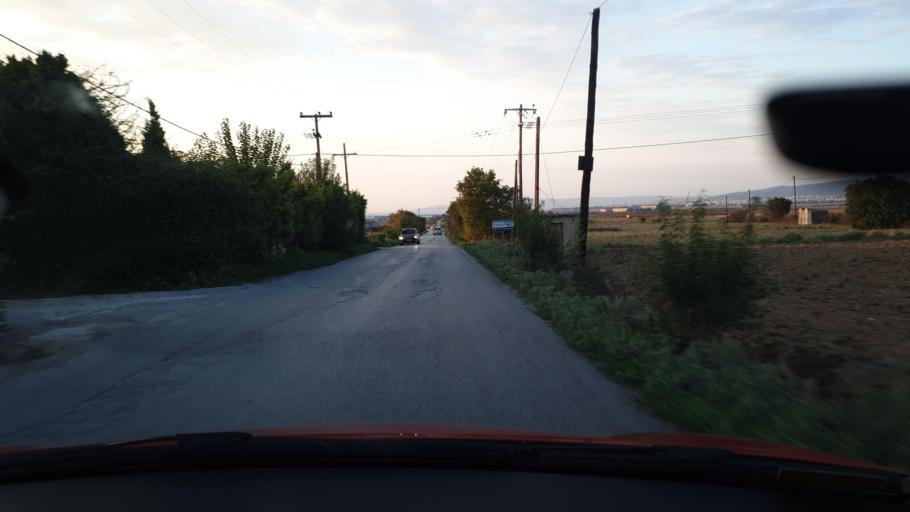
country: GR
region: Central Macedonia
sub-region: Nomos Thessalonikis
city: Peraia
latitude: 40.5052
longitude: 22.9487
